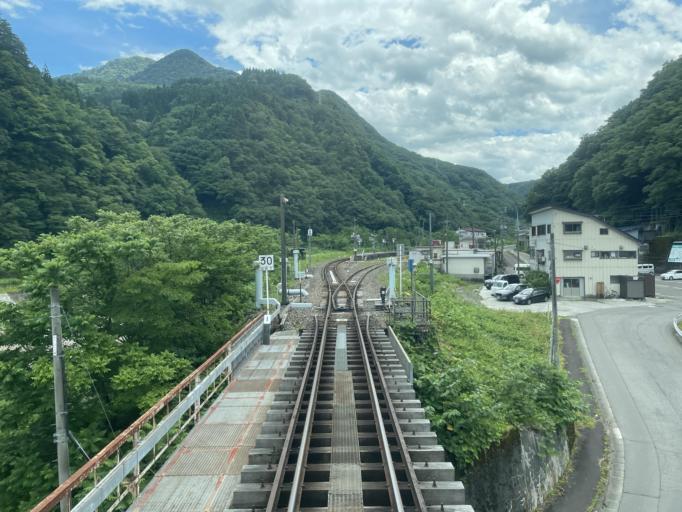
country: JP
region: Niigata
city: Itoigawa
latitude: 36.8878
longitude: 137.8647
